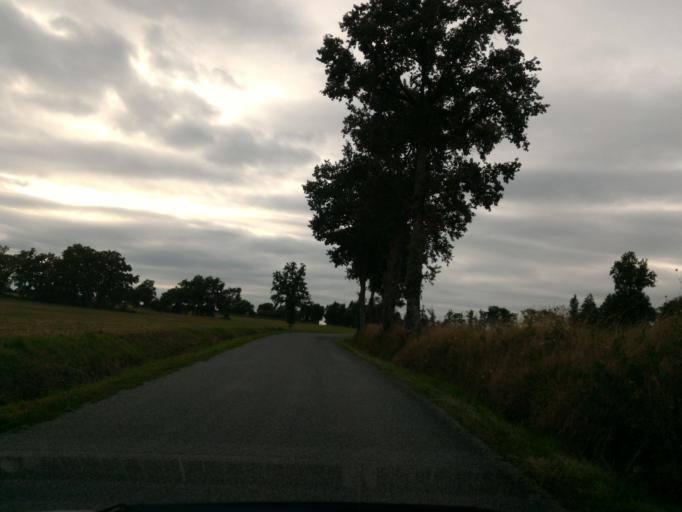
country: FR
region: Poitou-Charentes
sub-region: Departement de la Charente
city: Brigueuil
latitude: 45.9126
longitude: 0.8557
